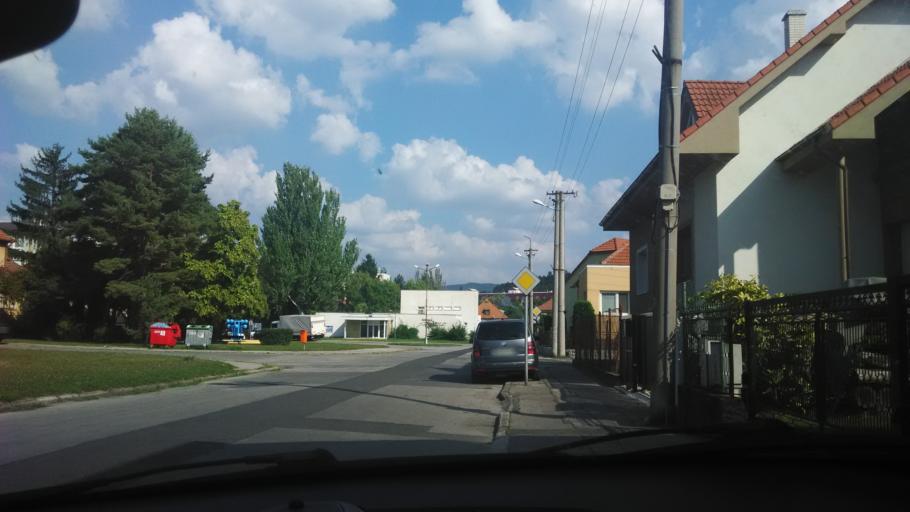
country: SK
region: Trnavsky
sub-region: Okres Trnava
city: Piestany
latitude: 48.5840
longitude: 17.8288
